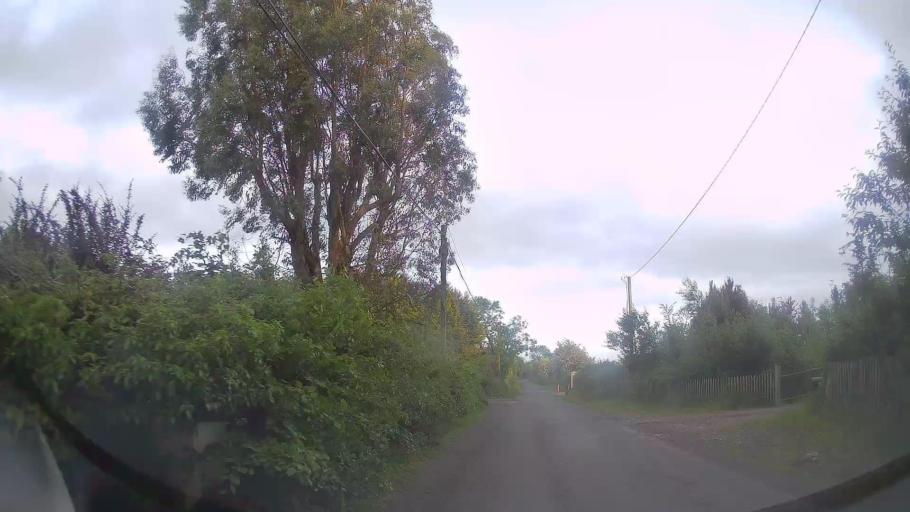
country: IE
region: Munster
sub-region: County Cork
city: Blarney
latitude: 51.9664
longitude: -8.5505
